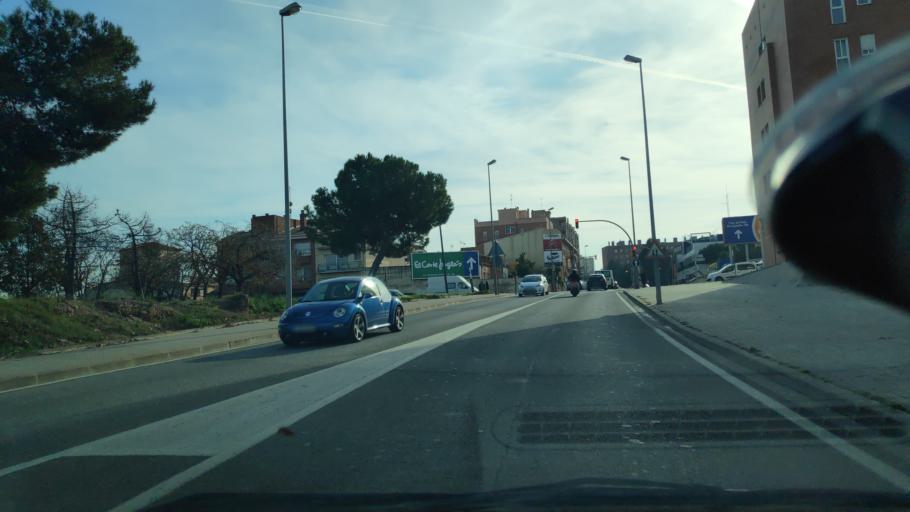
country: ES
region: Catalonia
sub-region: Provincia de Barcelona
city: Sabadell
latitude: 41.5652
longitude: 2.1010
